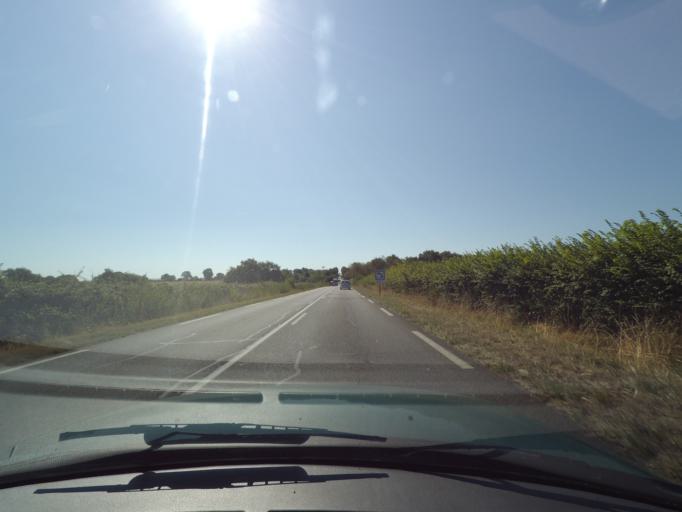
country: FR
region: Limousin
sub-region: Departement de la Haute-Vienne
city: Peyrat-de-Bellac
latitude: 46.1394
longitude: 0.9794
